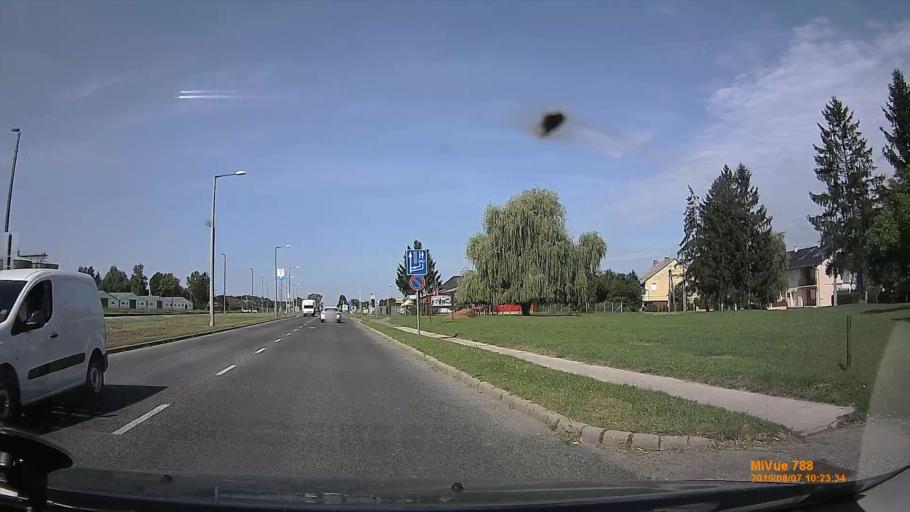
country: HU
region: Zala
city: Lenti
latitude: 46.6221
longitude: 16.5247
